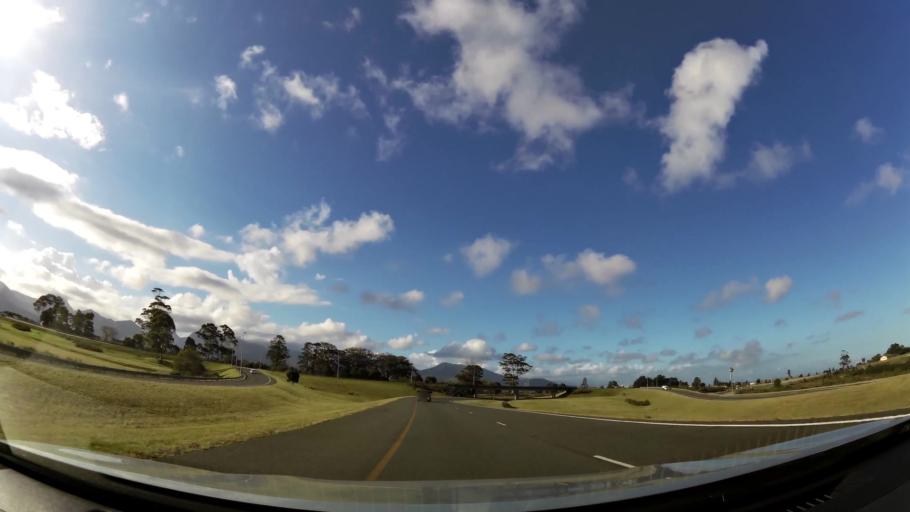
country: ZA
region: Western Cape
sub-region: Eden District Municipality
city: George
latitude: -33.9869
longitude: 22.5070
